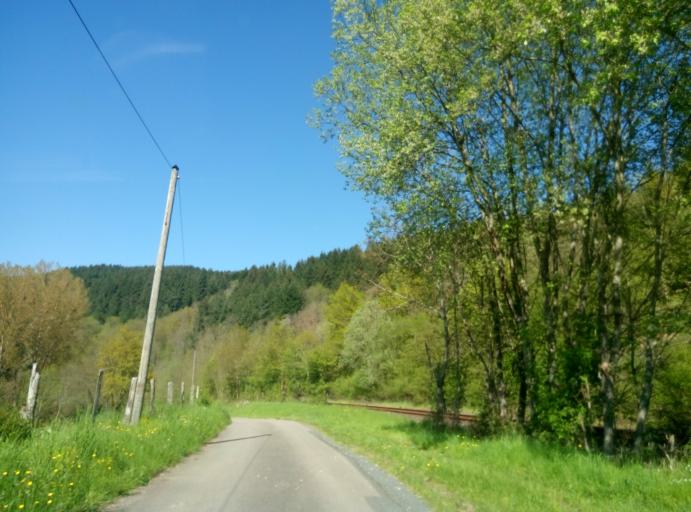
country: FR
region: Rhone-Alpes
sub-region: Departement du Rhone
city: Grandris
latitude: 46.0504
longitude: 4.4949
